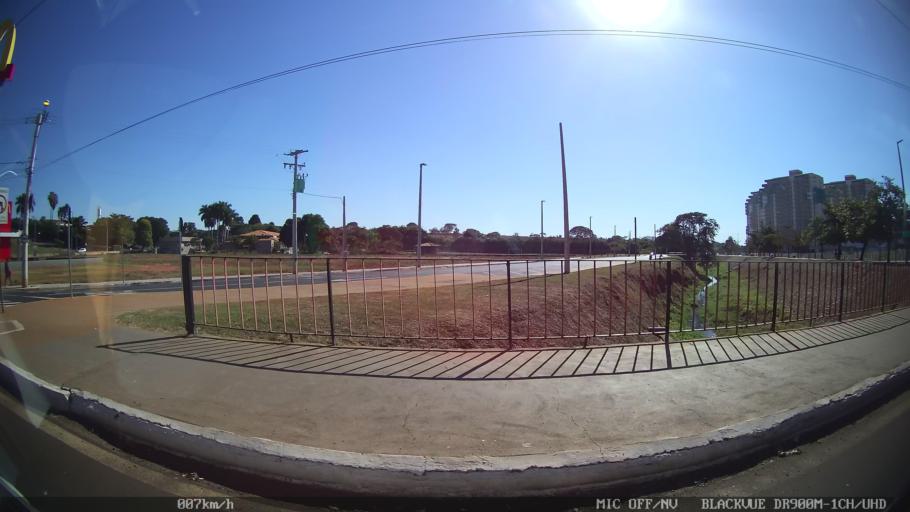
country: BR
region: Sao Paulo
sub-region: Olimpia
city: Olimpia
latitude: -20.7288
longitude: -48.9146
